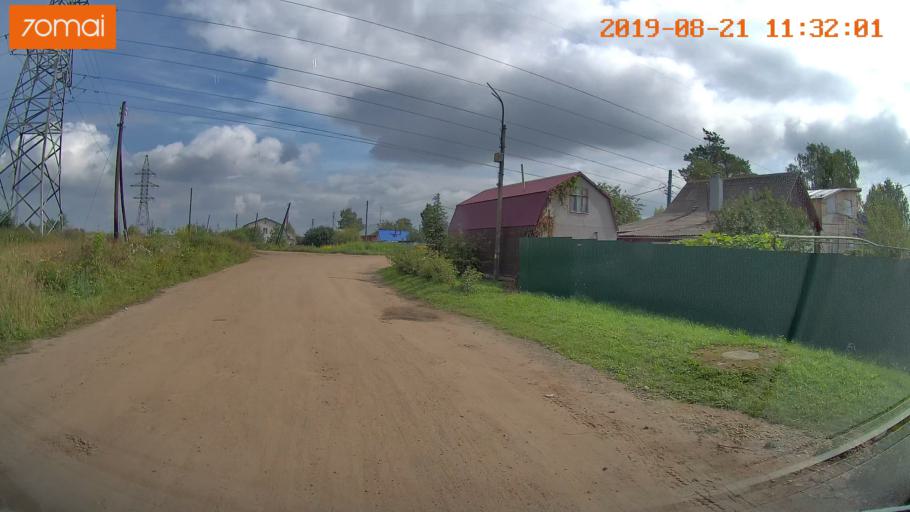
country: RU
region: Ivanovo
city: Novo-Talitsy
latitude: 56.9871
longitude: 40.9095
